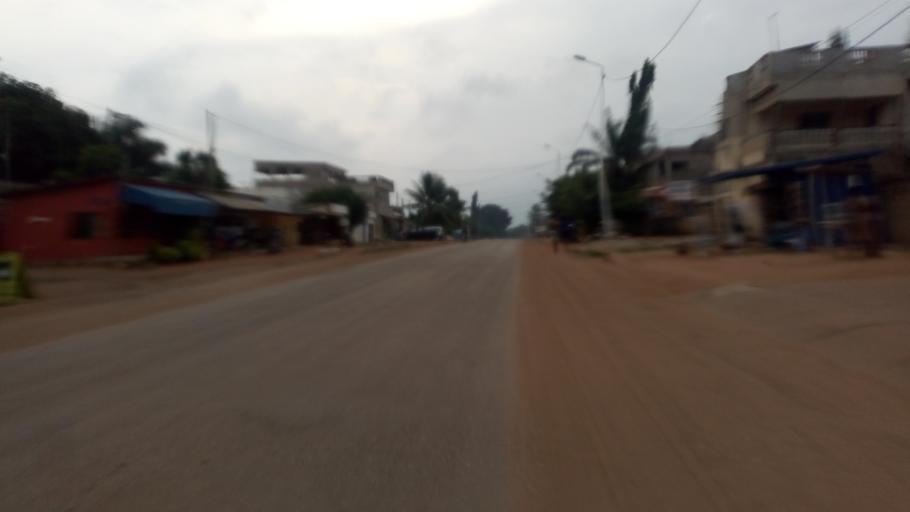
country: TG
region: Maritime
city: Lome
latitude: 6.1812
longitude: 1.1906
